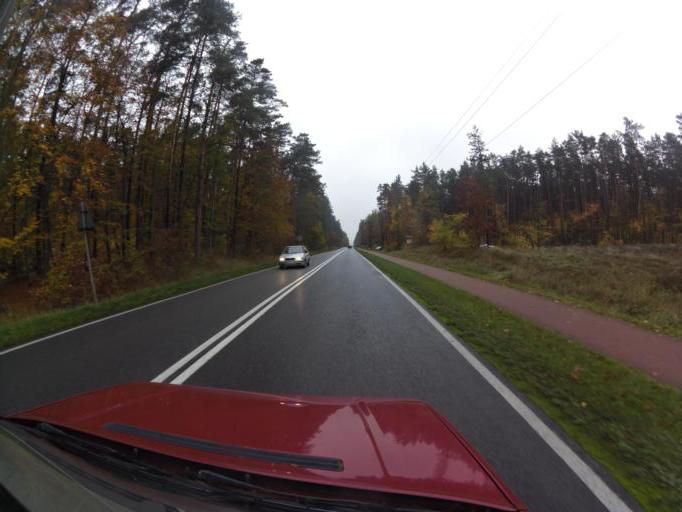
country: PL
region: West Pomeranian Voivodeship
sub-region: Powiat policki
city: Dobra
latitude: 53.5203
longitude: 14.4699
